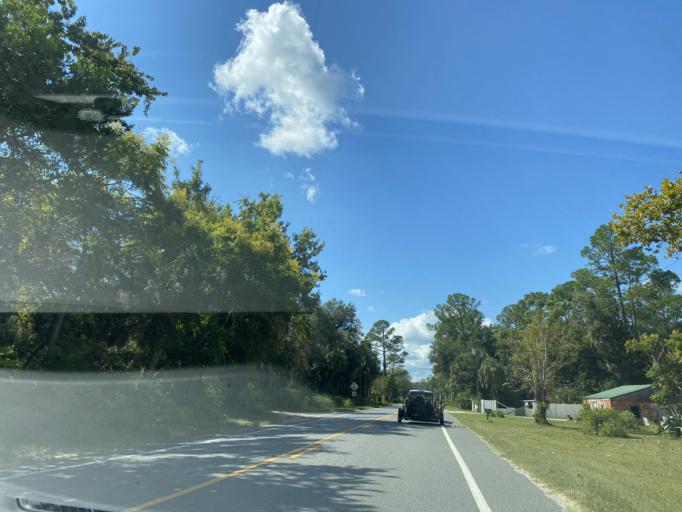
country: US
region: Florida
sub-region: Lake County
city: Lake Mack-Forest Hills
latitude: 29.0171
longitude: -81.4912
